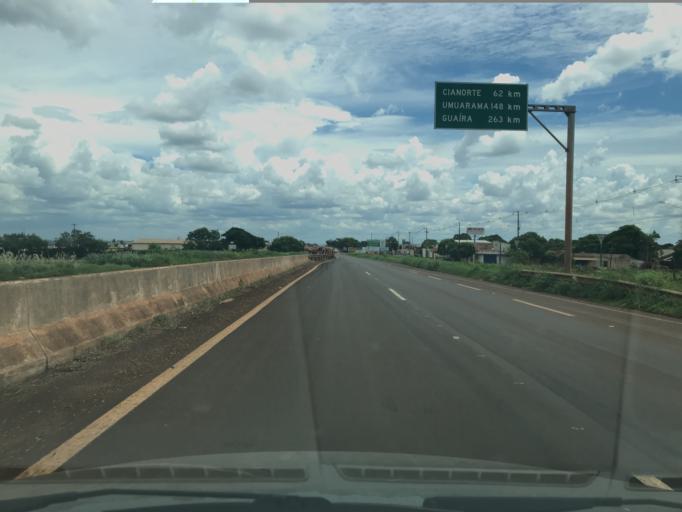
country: BR
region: Parana
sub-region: Paicandu
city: Paicandu
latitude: -23.4656
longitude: -52.0521
